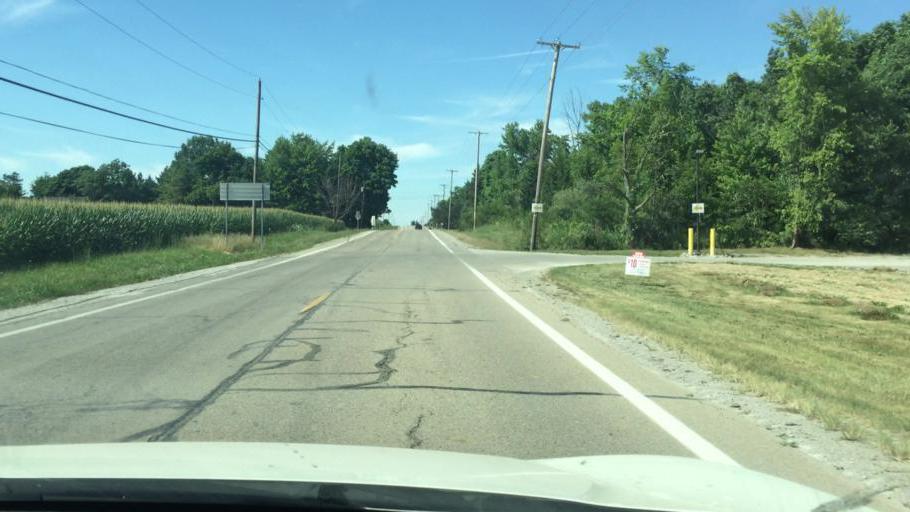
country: US
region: Ohio
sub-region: Clark County
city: Lisbon
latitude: 39.9357
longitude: -83.6117
